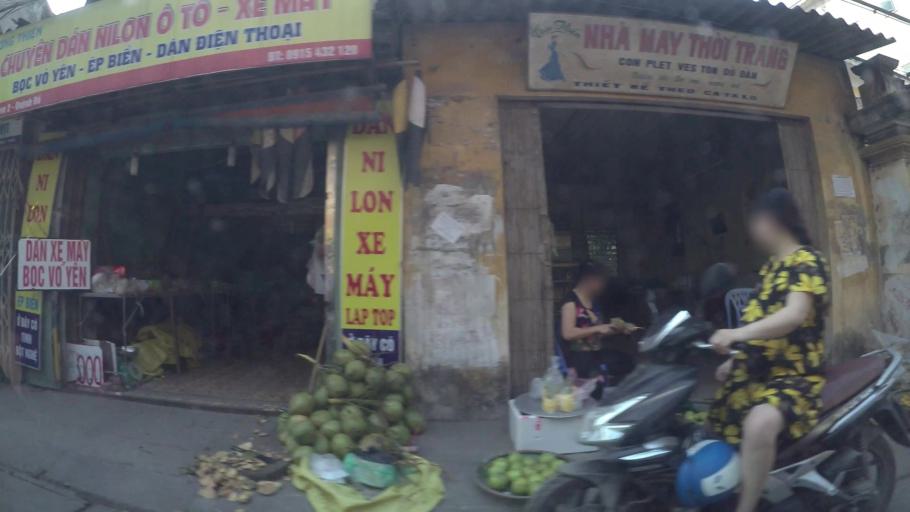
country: VN
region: Ha Noi
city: Van Dien
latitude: 20.9368
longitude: 105.8385
